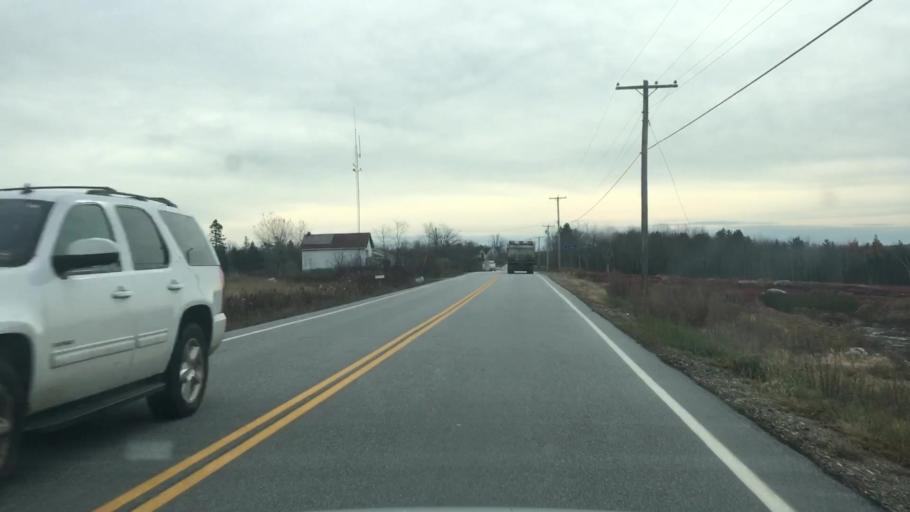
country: US
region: Maine
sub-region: Hancock County
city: Penobscot
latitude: 44.5258
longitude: -68.6651
